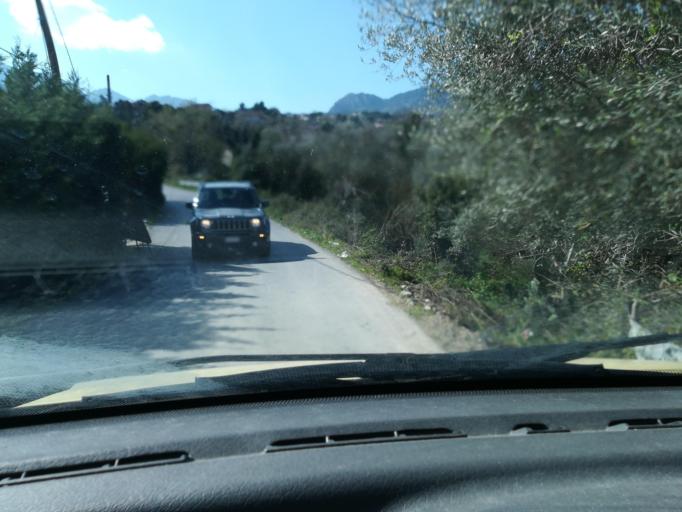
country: IT
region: Sicily
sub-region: Palermo
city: Cannizzaro-Favara
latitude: 38.0520
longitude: 13.2590
